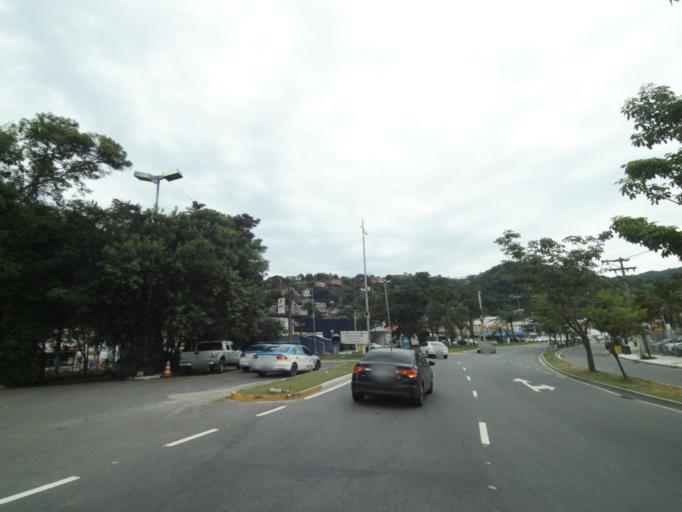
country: BR
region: Rio de Janeiro
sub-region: Niteroi
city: Niteroi
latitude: -22.9322
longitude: -43.0666
